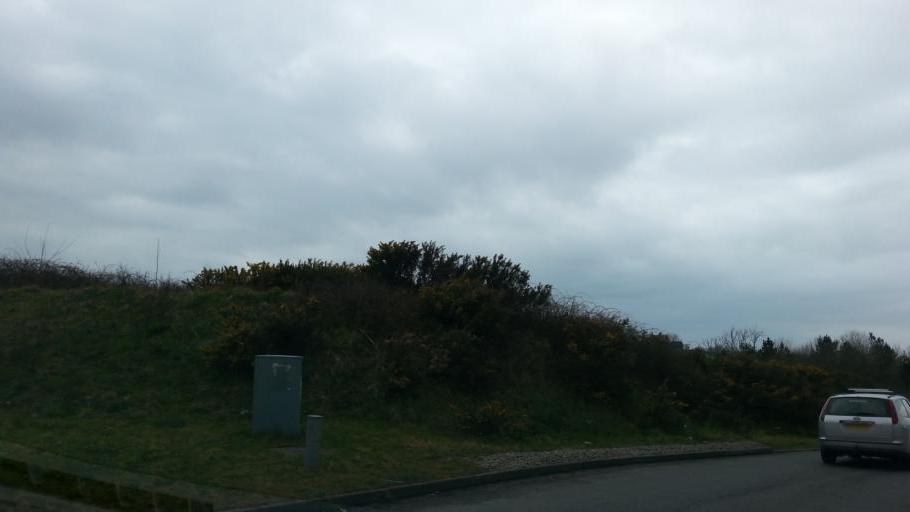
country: GB
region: England
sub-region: Devon
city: Appledore
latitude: 51.0305
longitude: -4.1923
